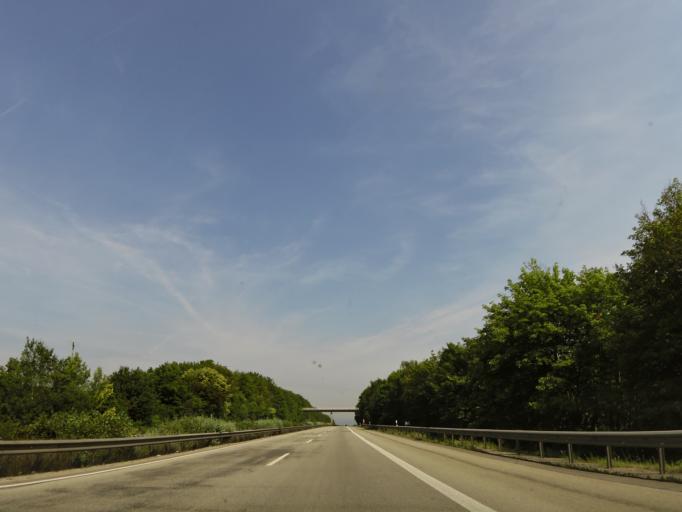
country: DE
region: Rheinland-Pfalz
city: Sprendlingen
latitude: 49.8514
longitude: 7.9787
